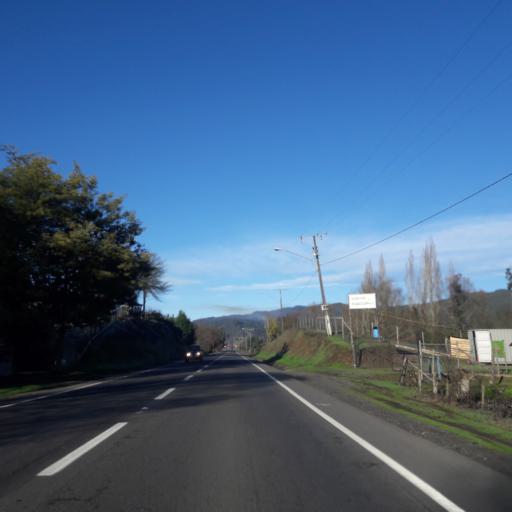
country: CL
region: Biobio
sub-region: Provincia de Concepcion
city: Lota
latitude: -37.2131
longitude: -72.9571
